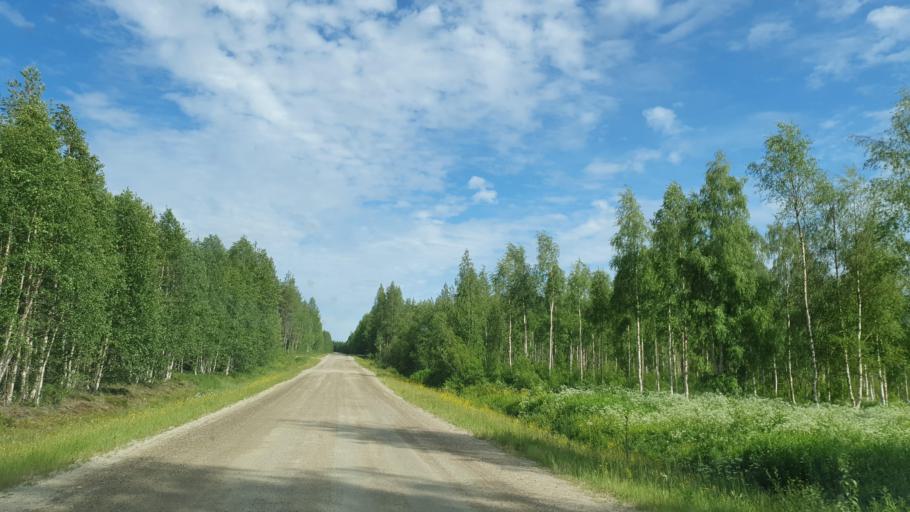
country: FI
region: Kainuu
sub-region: Kehys-Kainuu
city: Kuhmo
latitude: 64.5146
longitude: 29.4128
